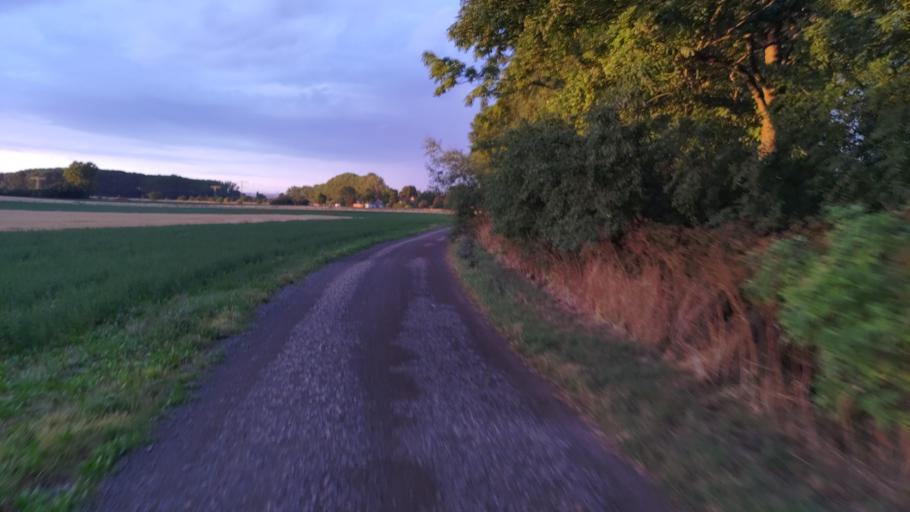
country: DE
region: Thuringia
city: Kleinmolsen
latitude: 50.9850
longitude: 11.0964
